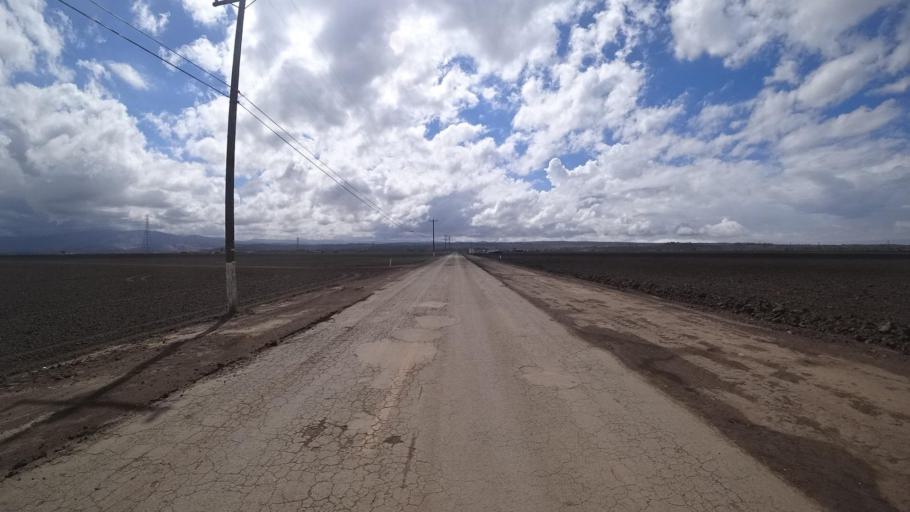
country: US
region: California
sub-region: Monterey County
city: Boronda
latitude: 36.6725
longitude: -121.7049
